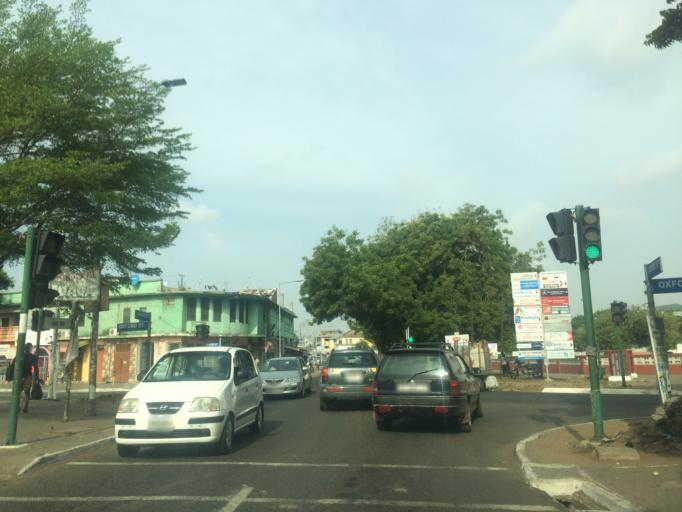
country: GH
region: Greater Accra
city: Accra
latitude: 5.5534
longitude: -0.1837
